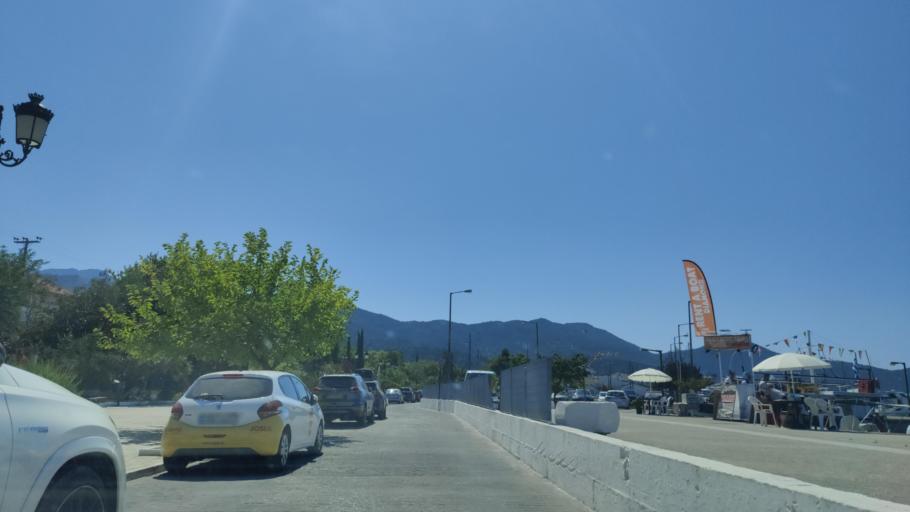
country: GR
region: East Macedonia and Thrace
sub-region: Nomos Kavalas
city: Thasos
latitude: 40.7796
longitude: 24.7080
